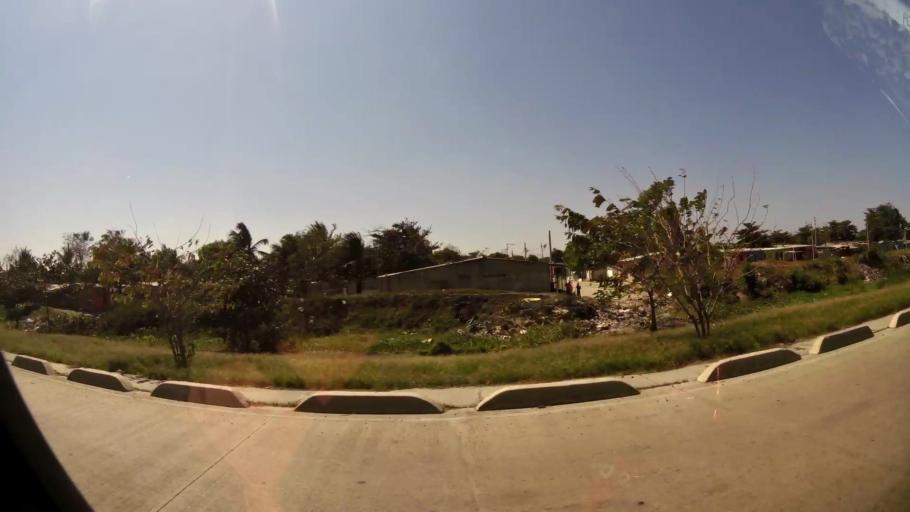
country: CO
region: Atlantico
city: Barranquilla
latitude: 10.9584
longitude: -74.7671
